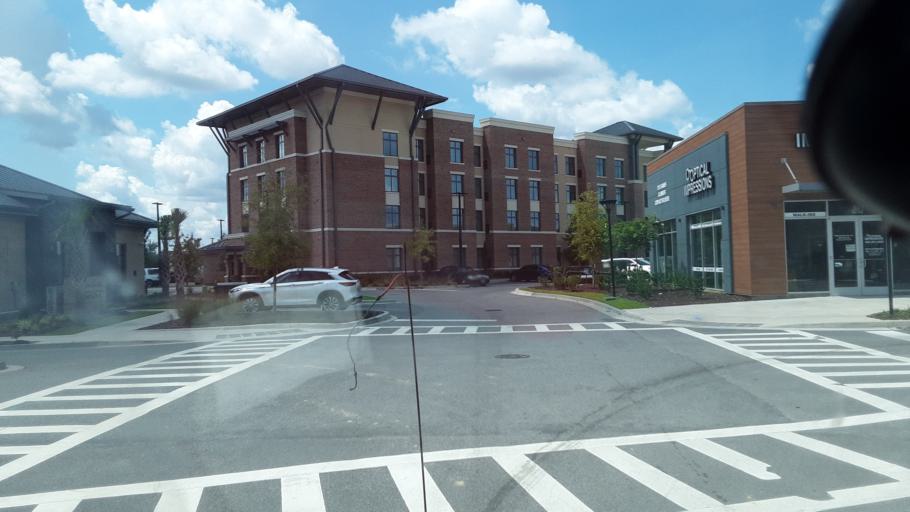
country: US
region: South Carolina
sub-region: Berkeley County
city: Sangaree
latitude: 33.0405
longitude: -80.1407
